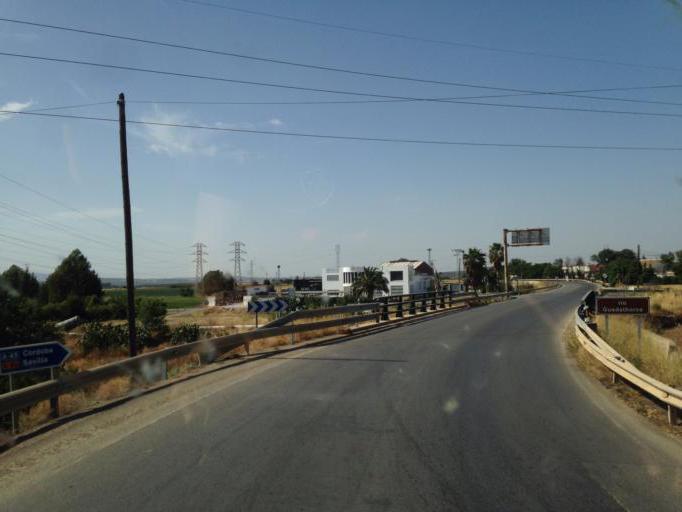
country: ES
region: Andalusia
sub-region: Provincia de Malaga
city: Antequera
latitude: 37.0517
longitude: -4.5627
